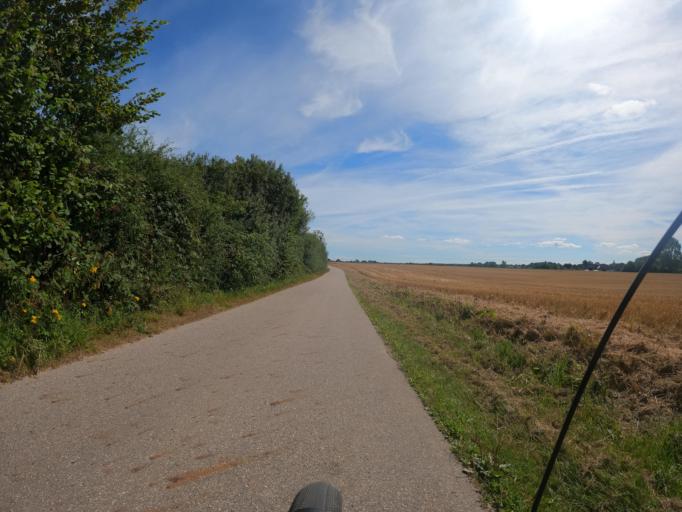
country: DE
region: Schleswig-Holstein
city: Steinbergkirche
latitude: 54.7638
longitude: 9.7608
